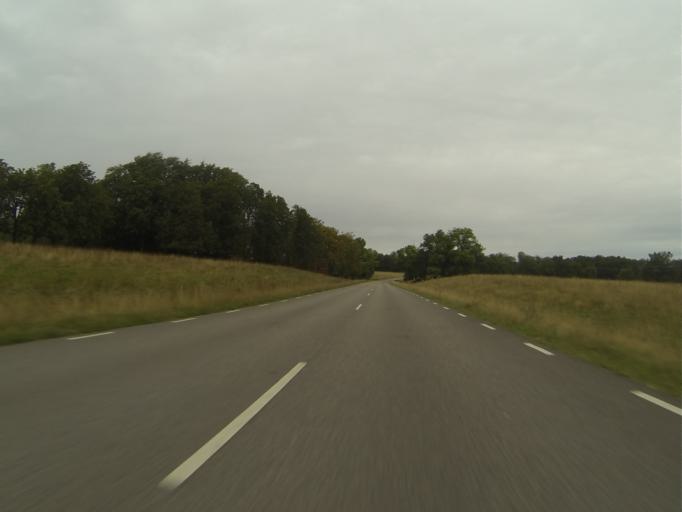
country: SE
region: Skane
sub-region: Lunds Kommun
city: Veberod
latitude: 55.6894
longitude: 13.4235
